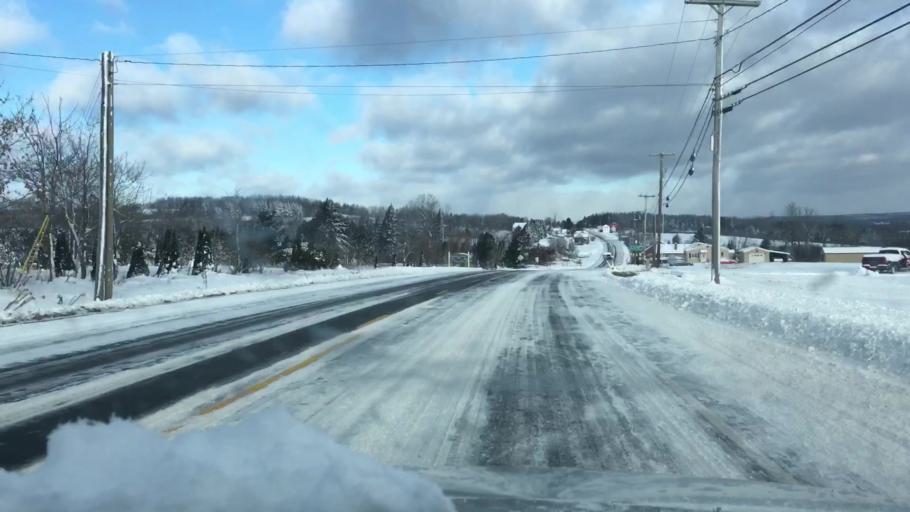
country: US
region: Maine
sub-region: Aroostook County
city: Caribou
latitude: 46.9543
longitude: -68.0271
